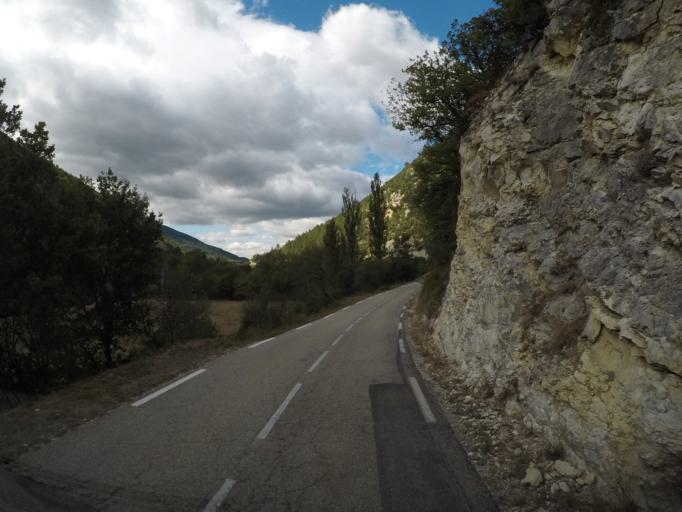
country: FR
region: Rhone-Alpes
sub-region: Departement de la Drome
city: Buis-les-Baronnies
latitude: 44.1866
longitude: 5.3451
